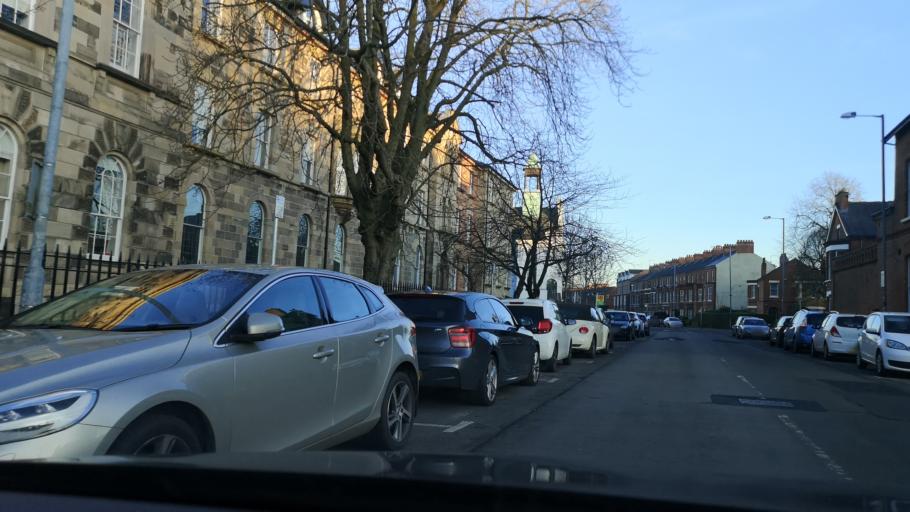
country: GB
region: Northern Ireland
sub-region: City of Belfast
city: Belfast
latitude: 54.5848
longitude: -5.9317
